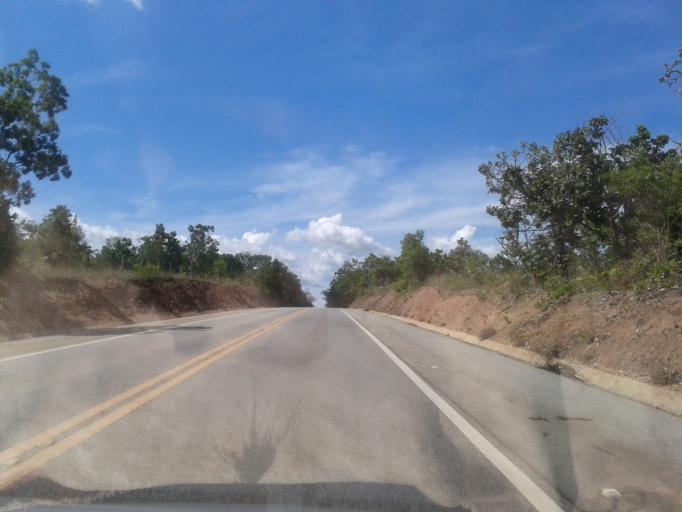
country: BR
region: Goias
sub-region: Goias
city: Goias
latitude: -15.7015
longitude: -50.1961
